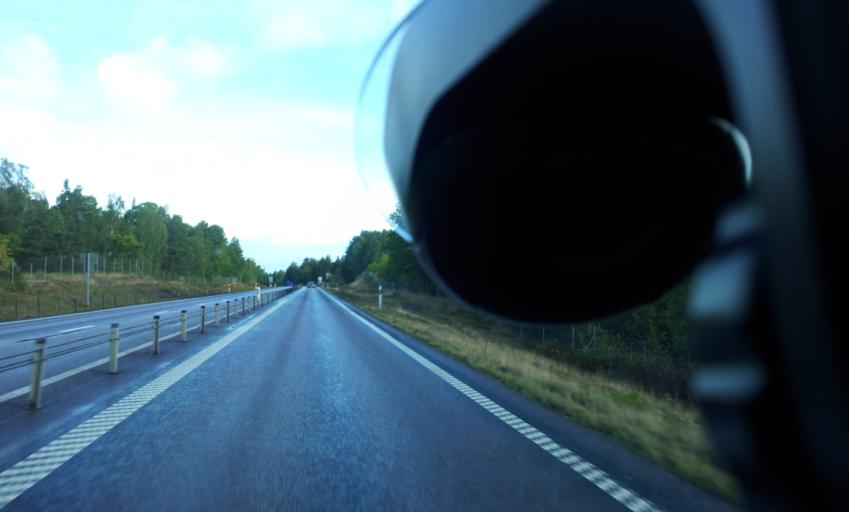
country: SE
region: Kalmar
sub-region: Oskarshamns Kommun
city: Paskallavik
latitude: 57.1421
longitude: 16.4700
